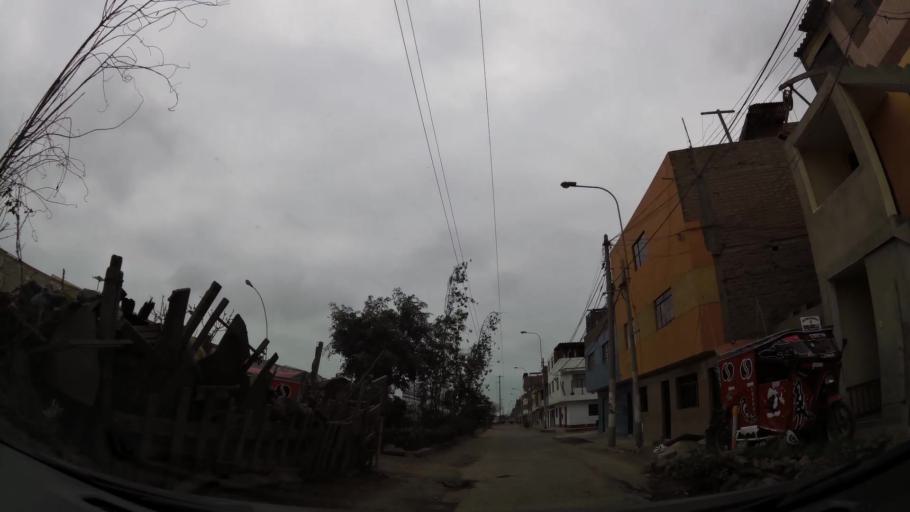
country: PE
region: Callao
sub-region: Callao
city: Callao
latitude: -12.0464
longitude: -77.1126
